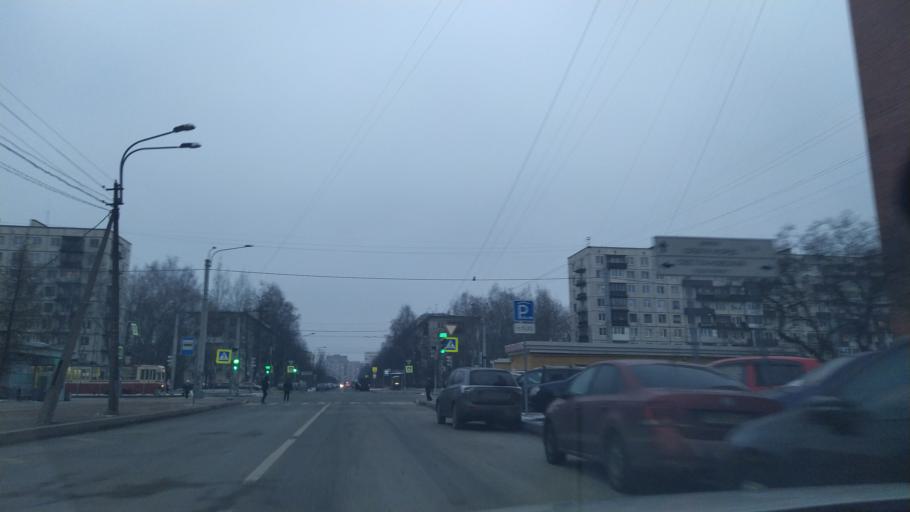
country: RU
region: St.-Petersburg
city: Grazhdanka
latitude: 60.0440
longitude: 30.4038
